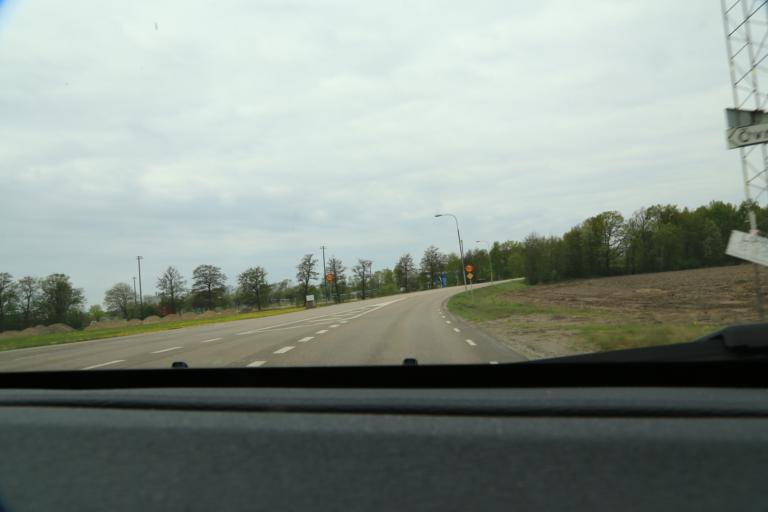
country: SE
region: Halland
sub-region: Varbergs Kommun
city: Tvaaker
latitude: 57.0453
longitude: 12.3836
